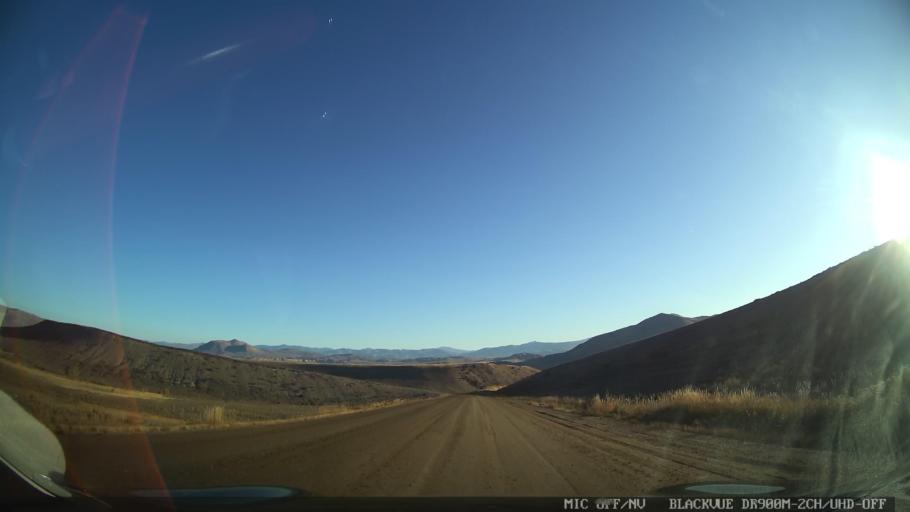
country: US
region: Colorado
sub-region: Grand County
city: Kremmling
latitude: 40.0096
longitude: -106.4011
